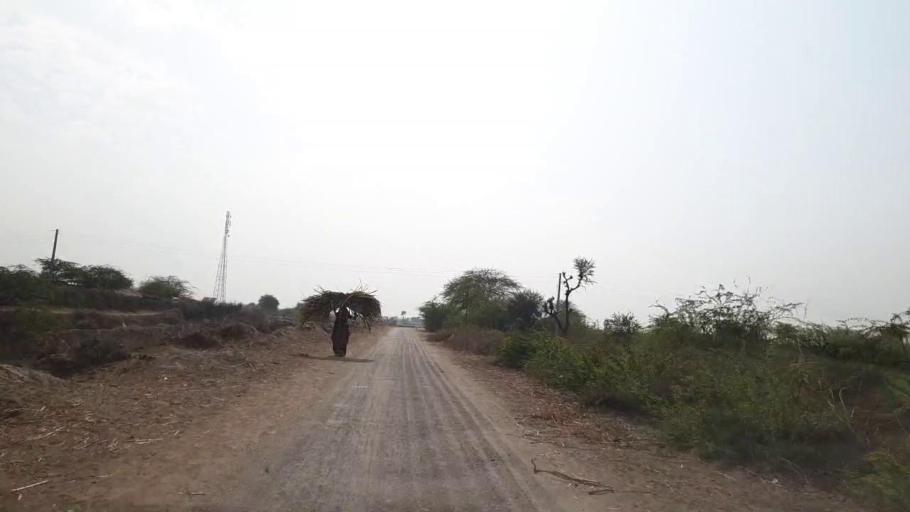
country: PK
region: Sindh
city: Mirpur Khas
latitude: 25.5430
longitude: 69.1623
